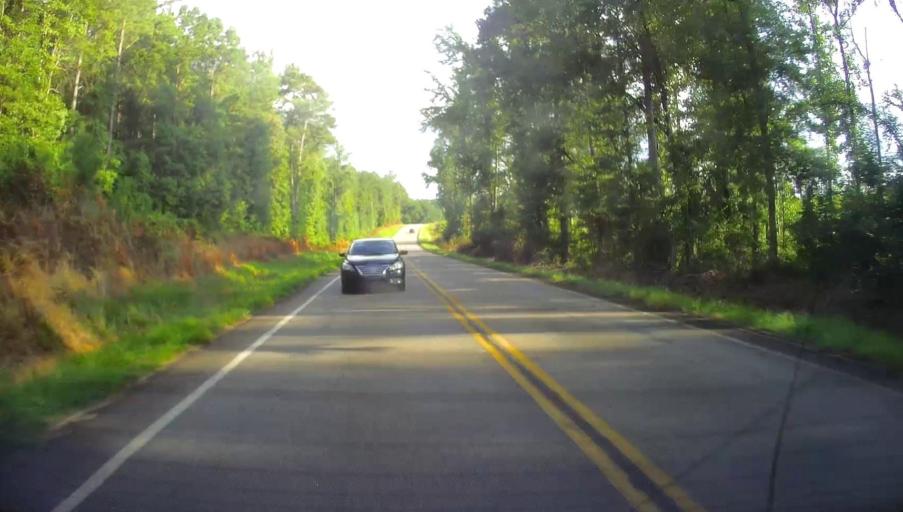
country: US
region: Georgia
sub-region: Crawford County
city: Knoxville
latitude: 32.8715
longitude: -83.9943
